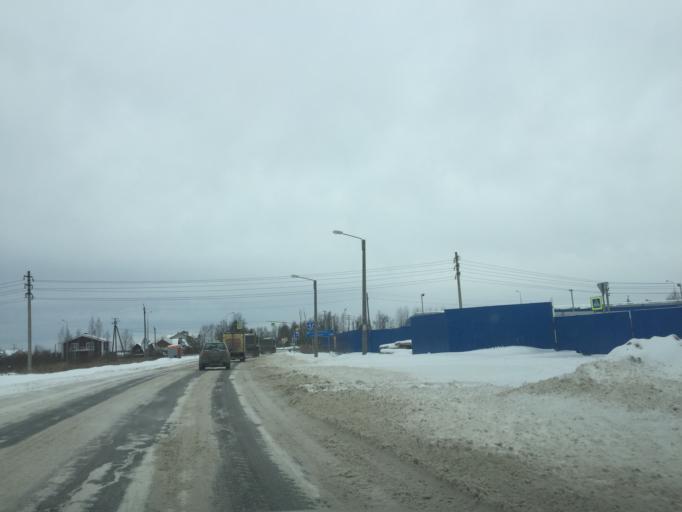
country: RU
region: Leningrad
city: Imeni Sverdlova
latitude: 59.7979
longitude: 30.6671
